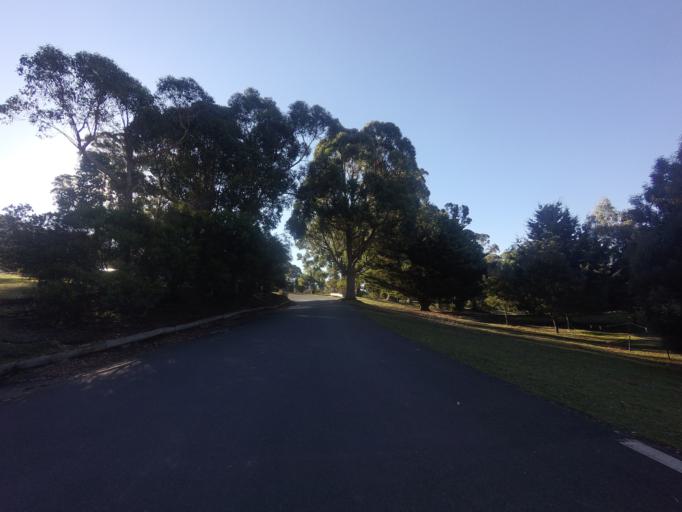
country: AU
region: Tasmania
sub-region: Glenorchy
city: Glenorchy
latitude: -42.8517
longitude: 147.2500
